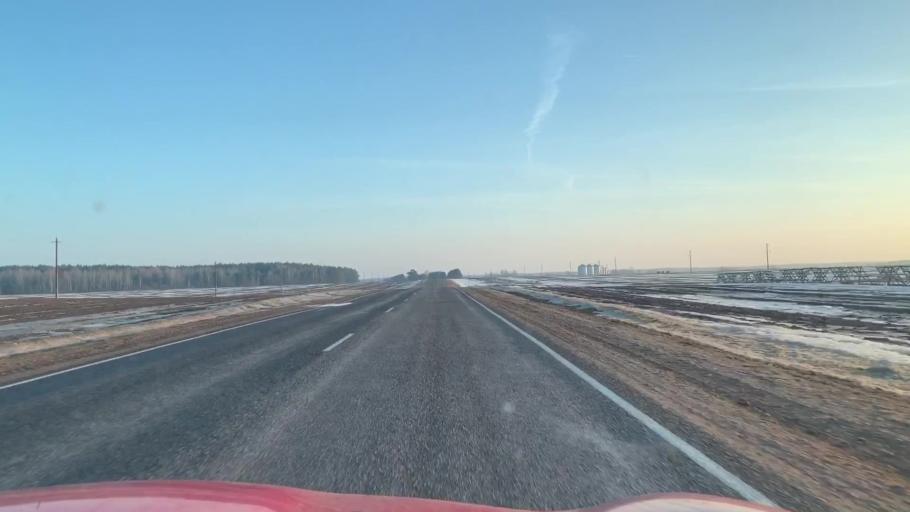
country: BY
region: Grodnenskaya
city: Mir
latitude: 53.4231
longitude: 26.4867
